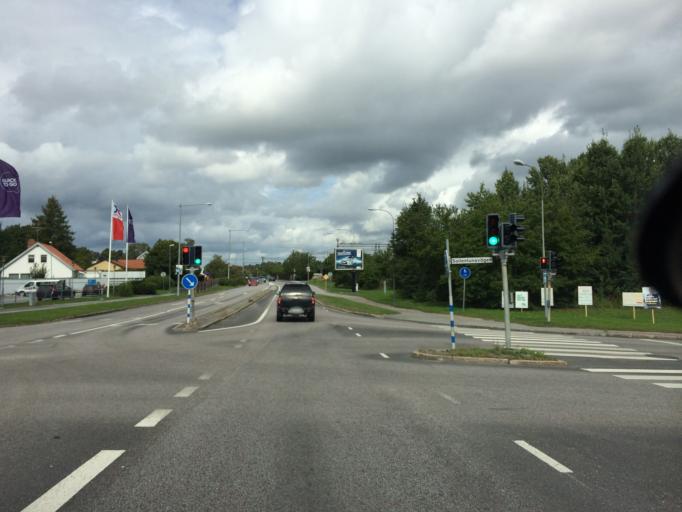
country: SE
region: Stockholm
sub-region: Sollentuna Kommun
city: Sollentuna
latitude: 59.4505
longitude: 17.9254
